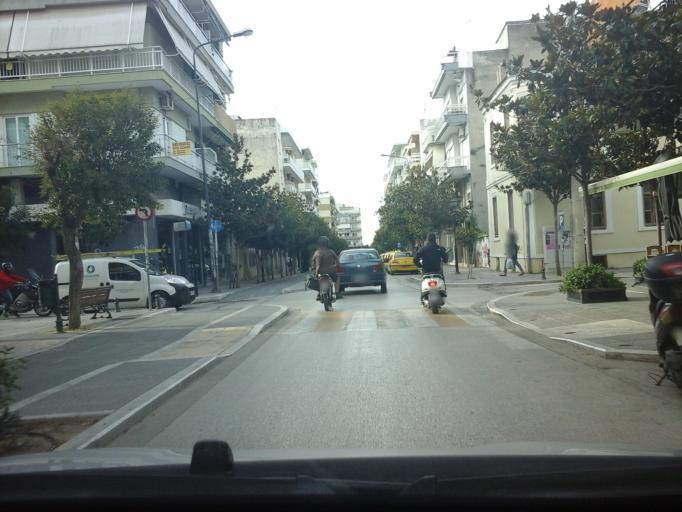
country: GR
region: East Macedonia and Thrace
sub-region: Nomos Evrou
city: Alexandroupoli
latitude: 40.8470
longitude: 25.8733
